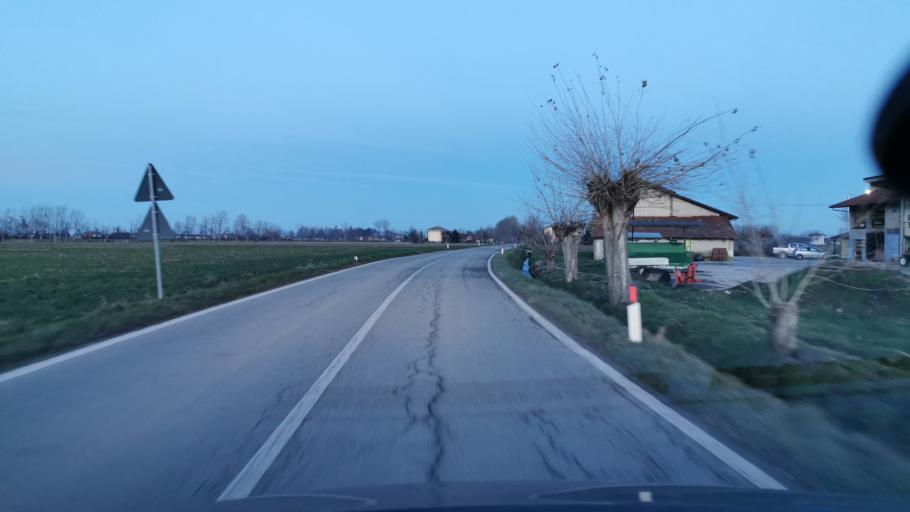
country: IT
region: Piedmont
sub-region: Provincia di Cuneo
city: Caraglio
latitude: 44.4457
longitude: 7.4723
